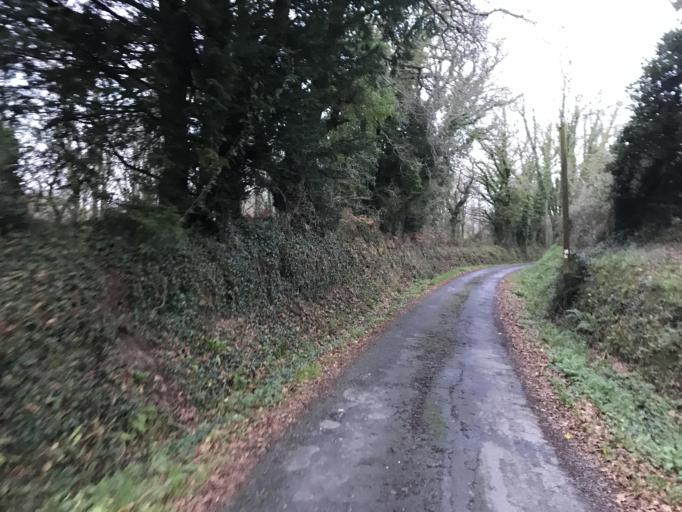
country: FR
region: Brittany
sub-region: Departement du Finistere
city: Loperhet
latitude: 48.3625
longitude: -4.3176
